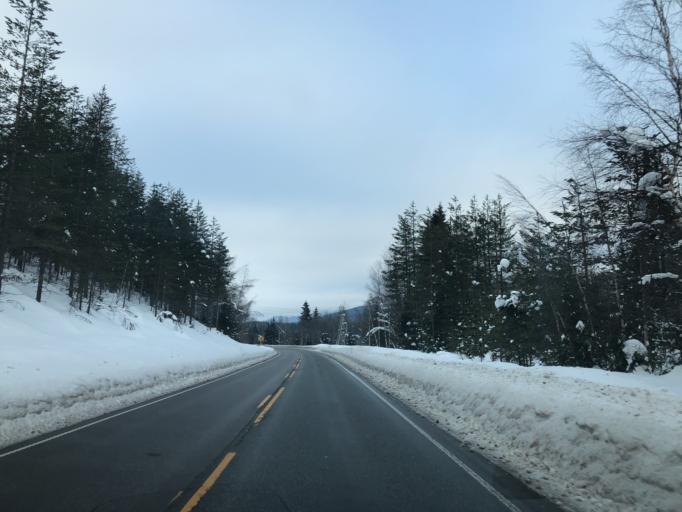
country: NO
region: Hedmark
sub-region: Trysil
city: Innbygda
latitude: 61.2671
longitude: 12.3062
